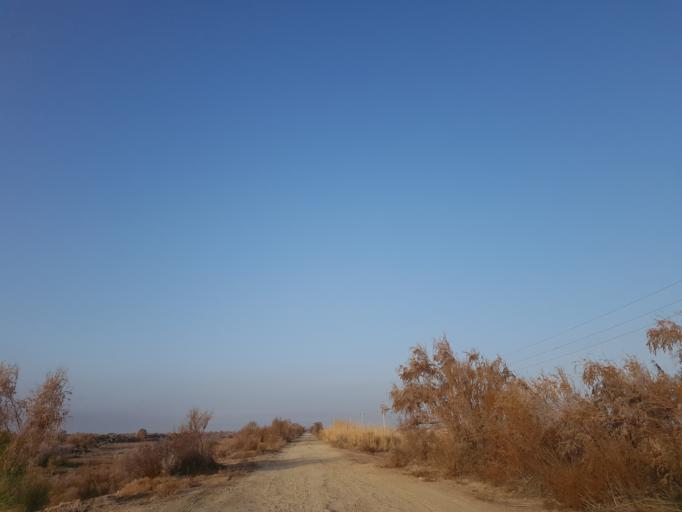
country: TM
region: Dasoguz
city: Koeneuergench
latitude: 41.8509
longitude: 58.2971
